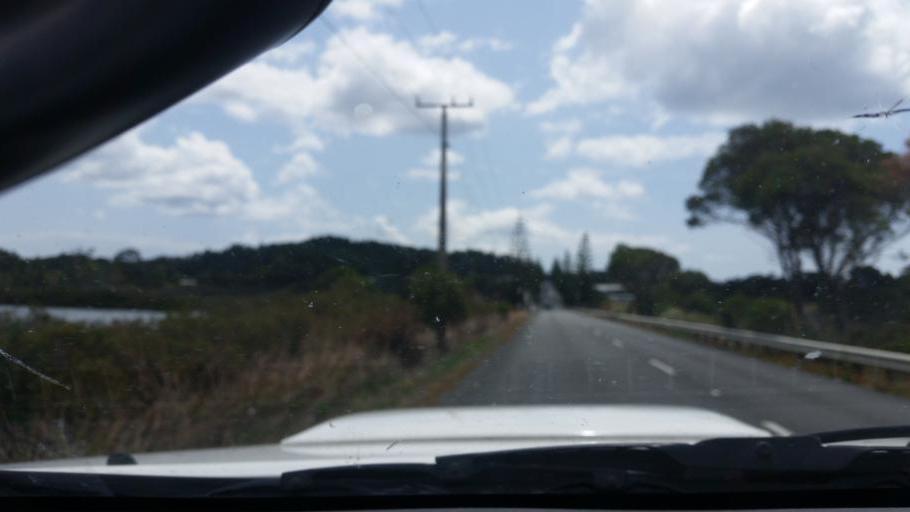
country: NZ
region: Auckland
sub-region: Auckland
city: Wellsford
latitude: -36.1095
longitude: 174.5782
